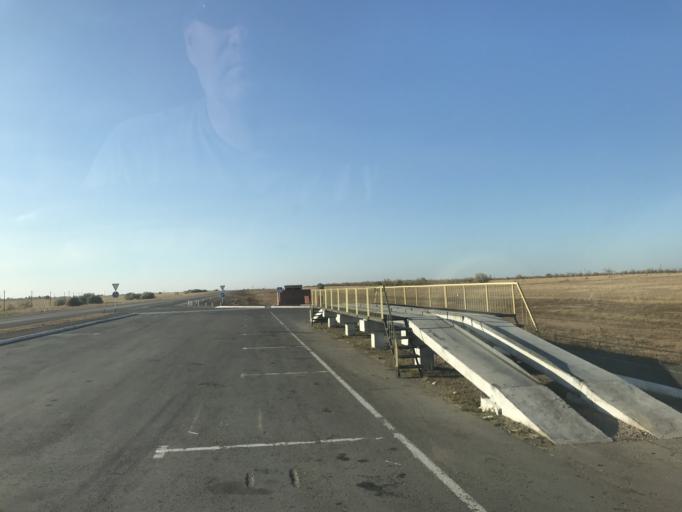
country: KZ
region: Pavlodar
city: Koktobe
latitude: 51.8827
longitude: 77.4190
